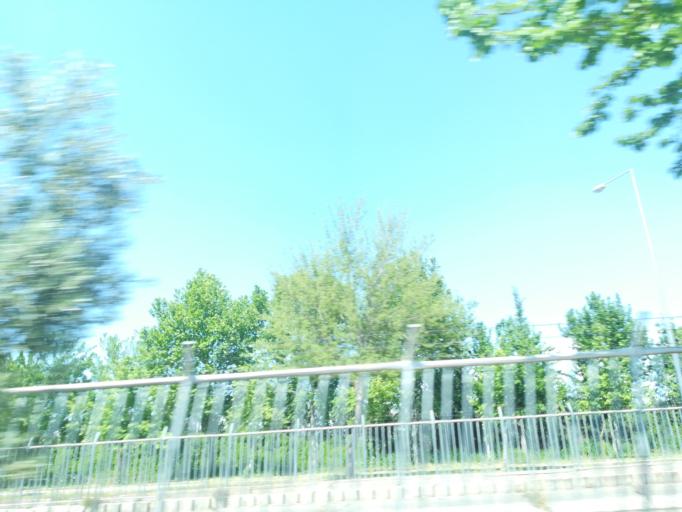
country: TR
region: Adana
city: Adana
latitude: 37.0243
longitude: 35.3663
